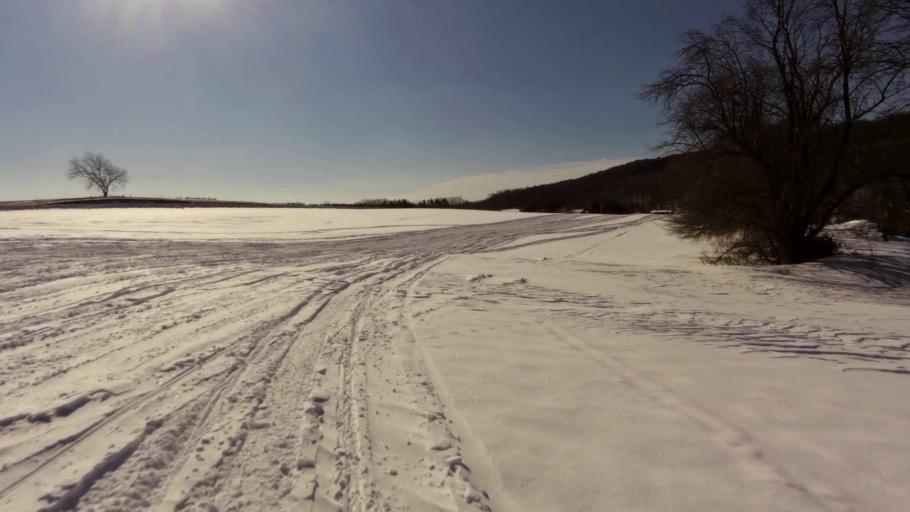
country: US
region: New York
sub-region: Cattaraugus County
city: Delevan
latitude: 42.4080
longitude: -78.5045
